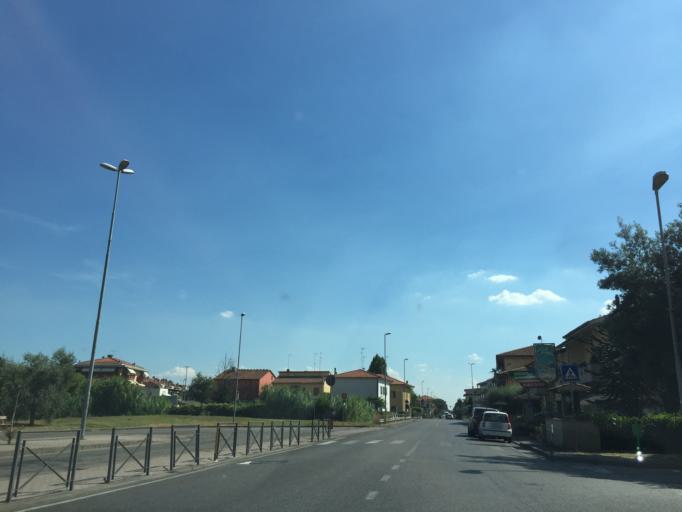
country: IT
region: Tuscany
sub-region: Provincia di Pistoia
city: Monsummano Terme
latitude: 43.8756
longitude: 10.8119
